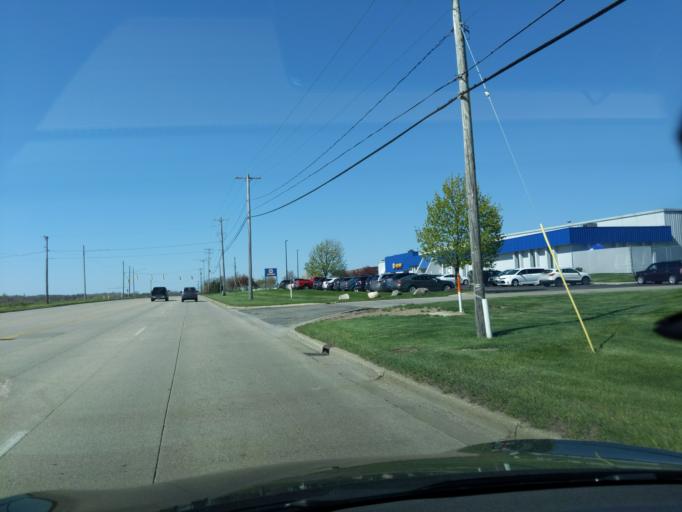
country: US
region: Michigan
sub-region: Kent County
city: East Grand Rapids
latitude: 42.9009
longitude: -85.5481
